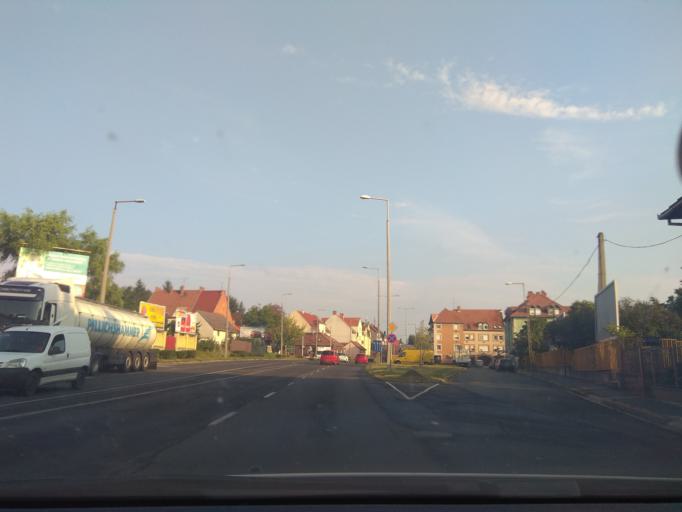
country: HU
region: Heves
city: Eger
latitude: 47.8952
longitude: 20.3690
